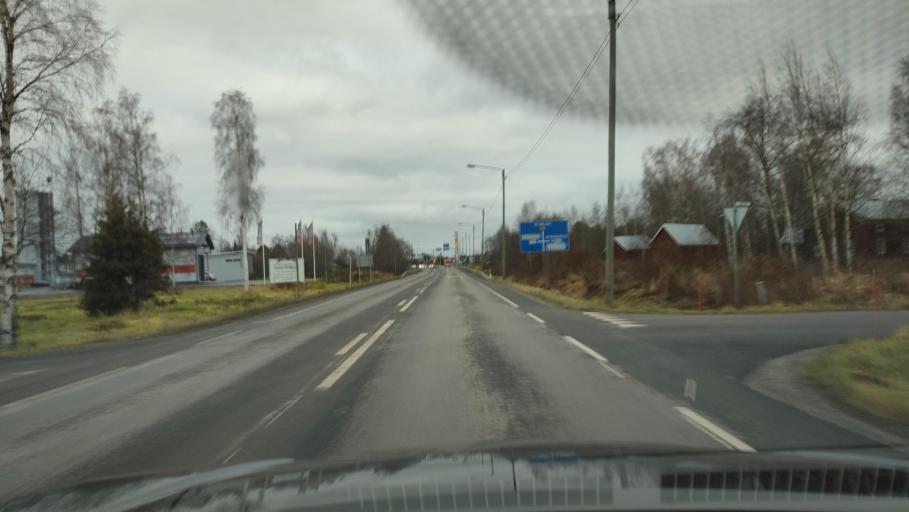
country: FI
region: Southern Ostrobothnia
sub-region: Seinaejoki
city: Ilmajoki
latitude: 62.7280
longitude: 22.5899
